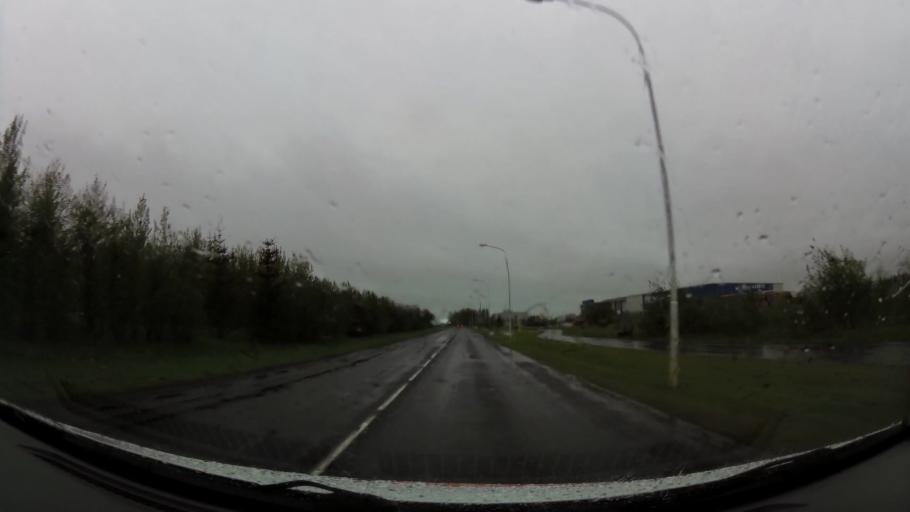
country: IS
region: South
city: Selfoss
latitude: 63.9357
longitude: -20.9790
